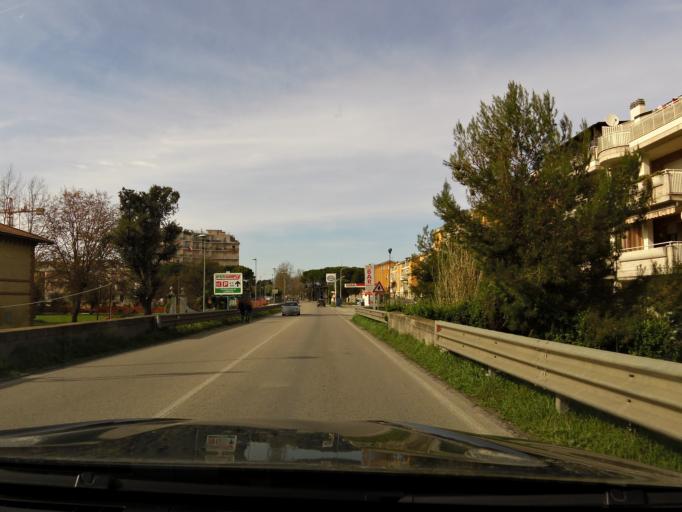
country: IT
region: The Marches
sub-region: Provincia di Macerata
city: Porto Recanati
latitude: 43.4241
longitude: 13.6641
